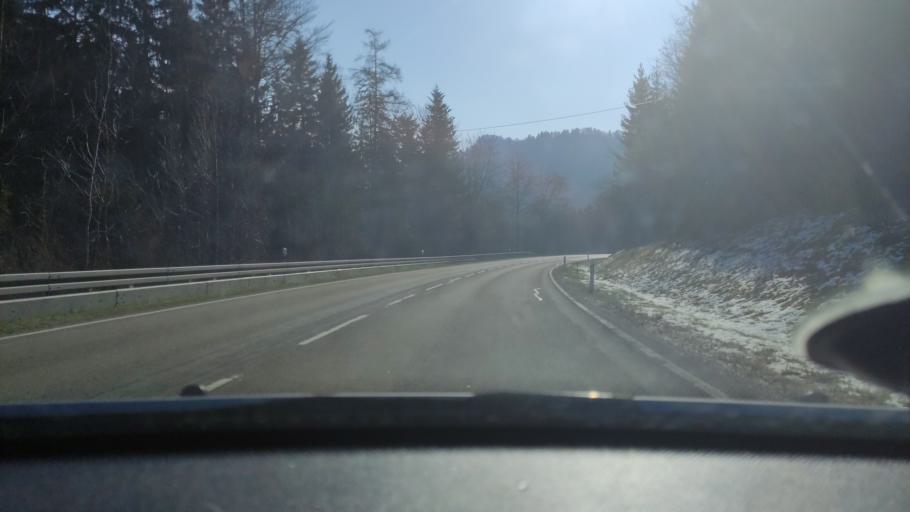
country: DE
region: Baden-Wuerttemberg
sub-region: Tuebingen Region
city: Hausen am Tann
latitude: 48.2245
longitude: 8.8525
